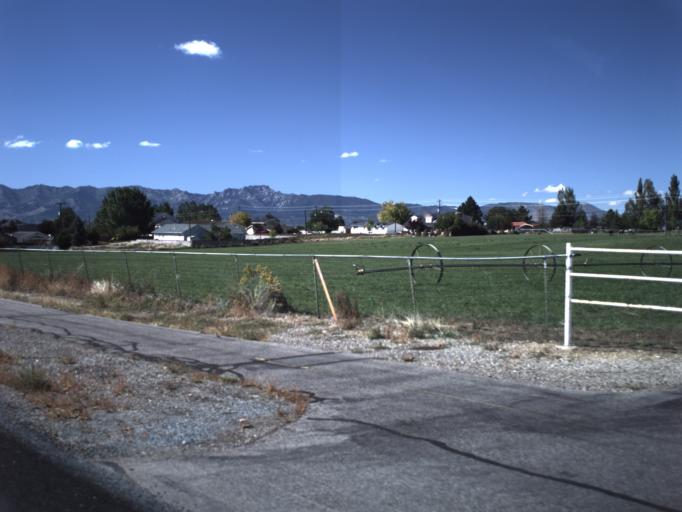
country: US
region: Utah
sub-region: Beaver County
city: Beaver
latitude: 38.2771
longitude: -112.6172
